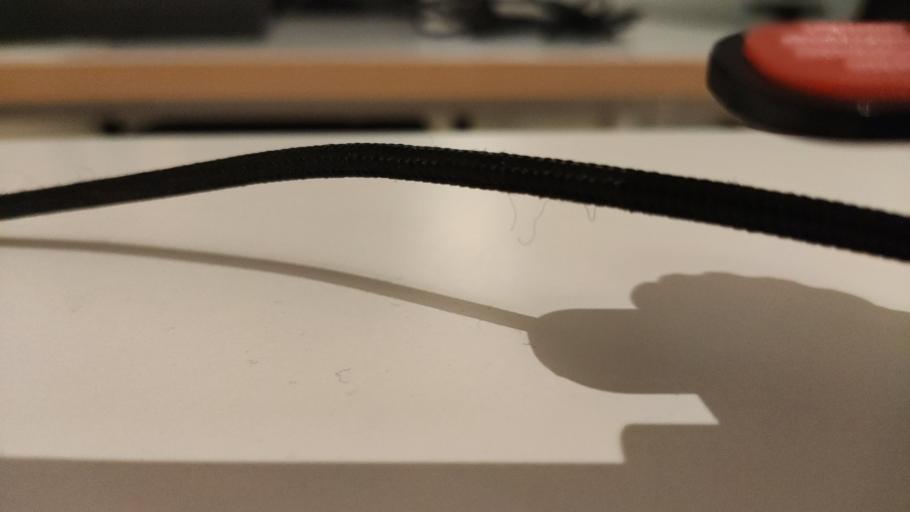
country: RU
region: Moskovskaya
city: Shaburnovo
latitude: 56.4325
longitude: 37.9344
